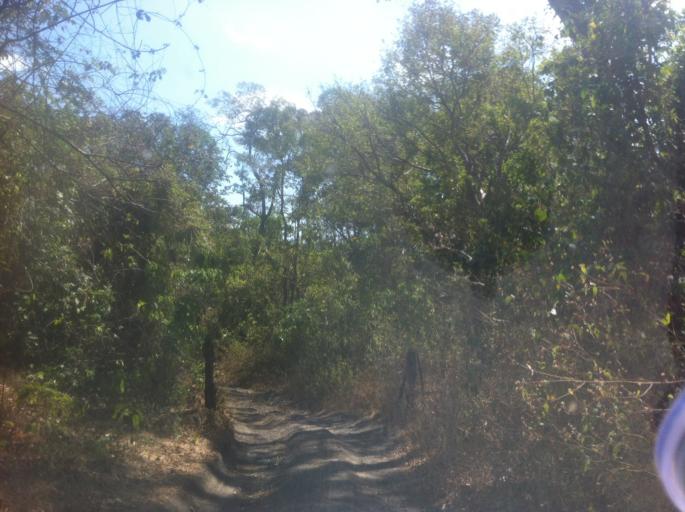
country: NI
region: Chinandega
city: Chichigalpa
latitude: 12.6942
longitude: -87.0283
